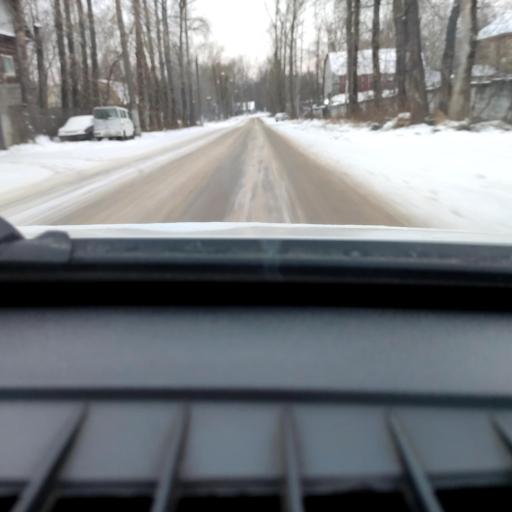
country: RU
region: Perm
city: Perm
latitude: 58.0973
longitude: 56.3694
